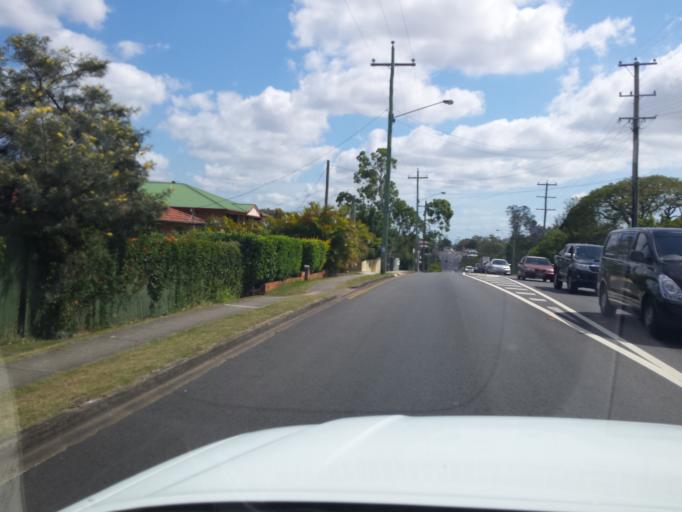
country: AU
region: Queensland
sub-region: Brisbane
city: Zillmere
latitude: -27.3719
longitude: 153.0358
